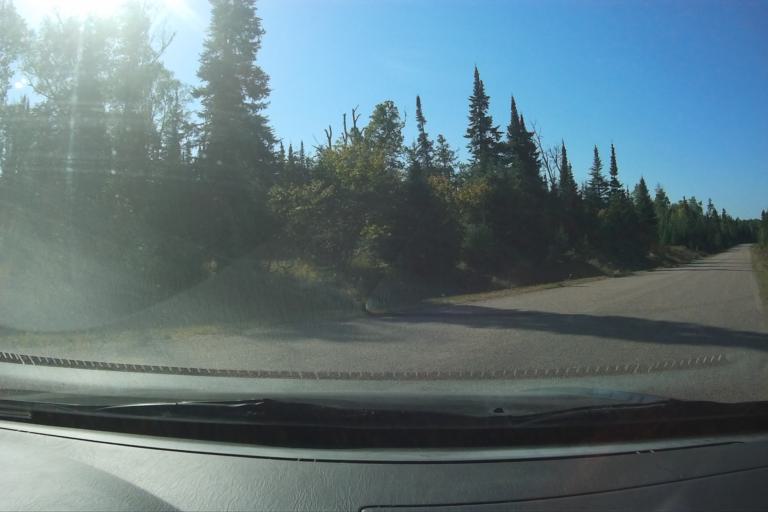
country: CA
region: Ontario
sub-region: Thunder Bay District
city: Thunder Bay
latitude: 48.3599
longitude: -88.7975
